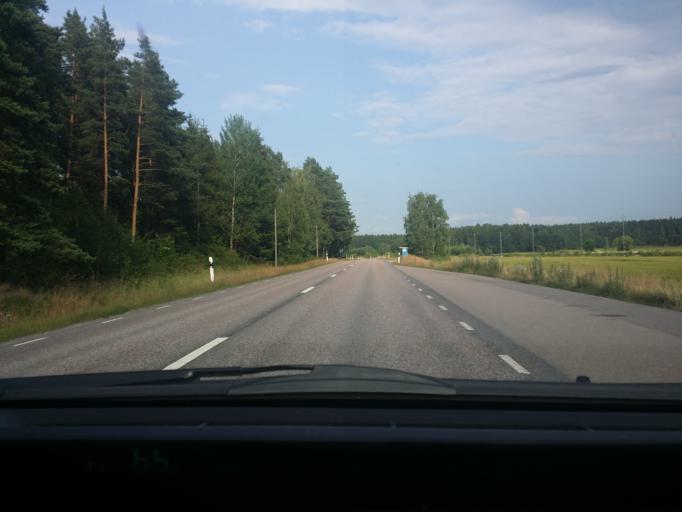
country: SE
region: Vaestmanland
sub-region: Hallstahammars Kommun
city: Kolback
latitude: 59.5662
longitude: 16.3574
